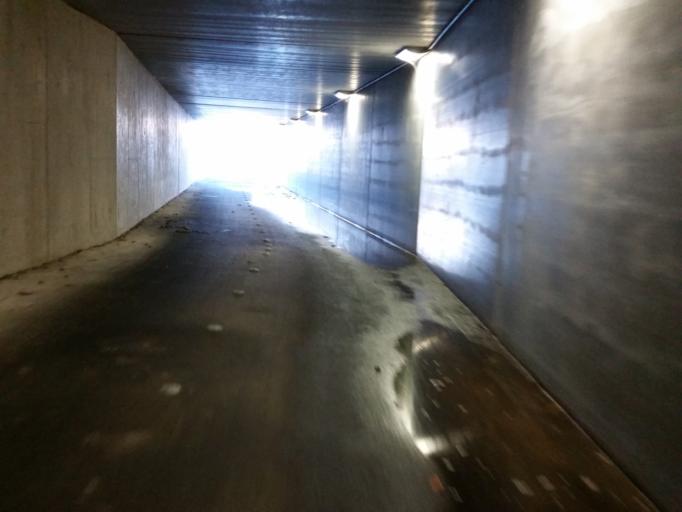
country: BE
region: Flanders
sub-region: Provincie Vlaams-Brabant
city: Haacht
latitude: 50.9472
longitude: 4.6422
